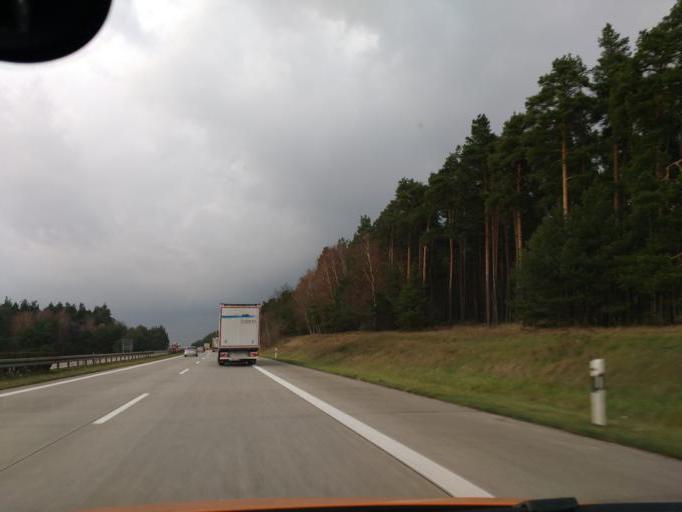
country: DE
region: Brandenburg
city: Heiligengrabe
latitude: 53.1615
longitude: 12.3867
